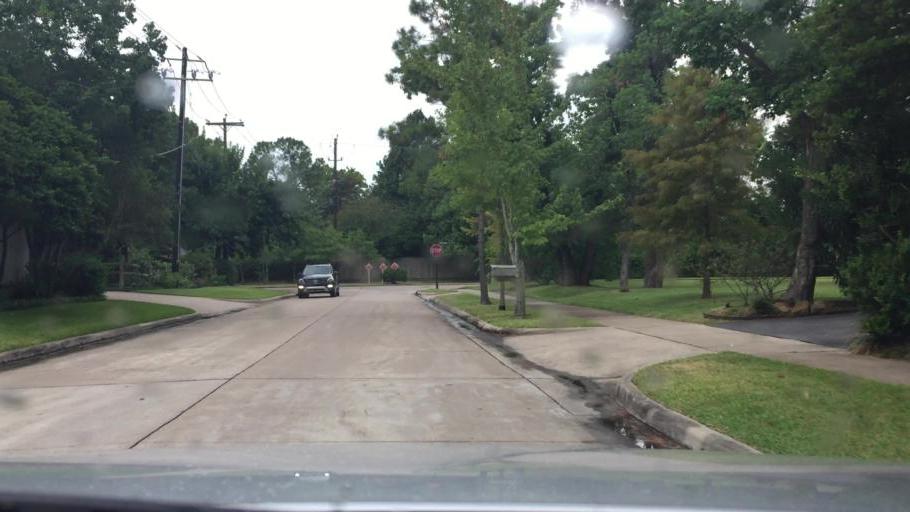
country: US
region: Texas
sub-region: Harris County
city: Piney Point Village
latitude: 29.7632
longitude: -95.5088
